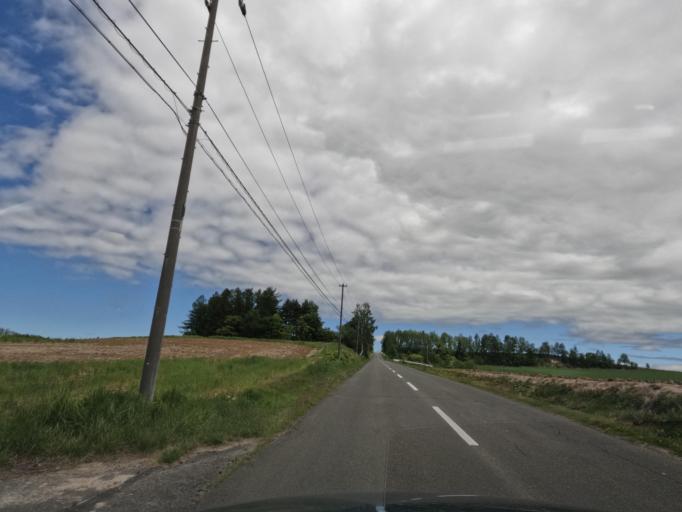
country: JP
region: Hokkaido
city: Shimo-furano
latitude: 43.5169
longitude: 142.4272
